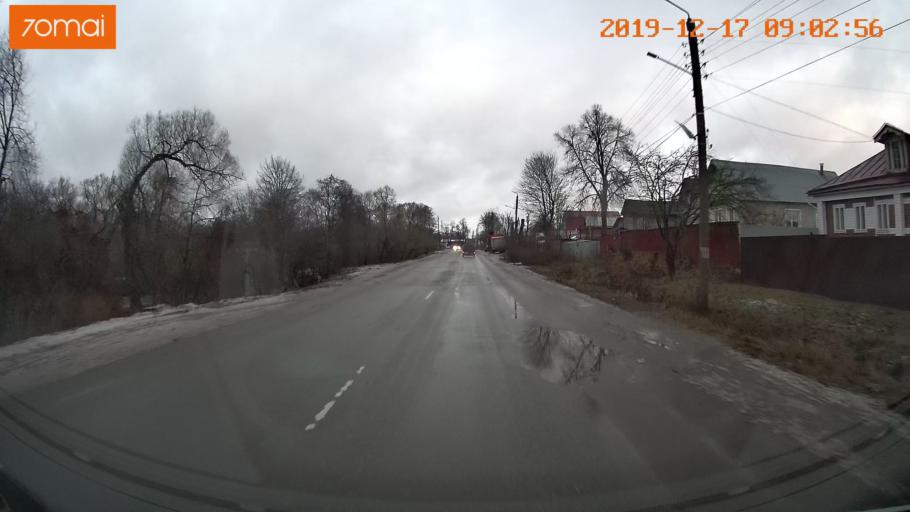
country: RU
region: Vladimir
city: Kosterevo
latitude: 55.9539
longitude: 39.6330
